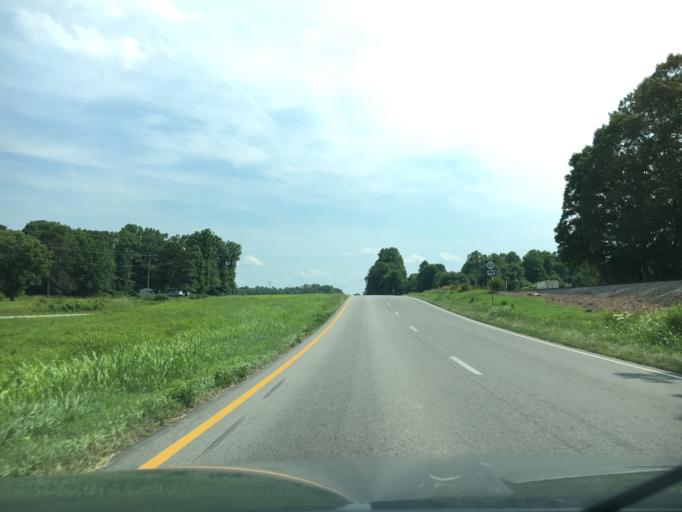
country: US
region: Virginia
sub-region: Nottoway County
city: Crewe
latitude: 37.2548
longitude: -78.1400
